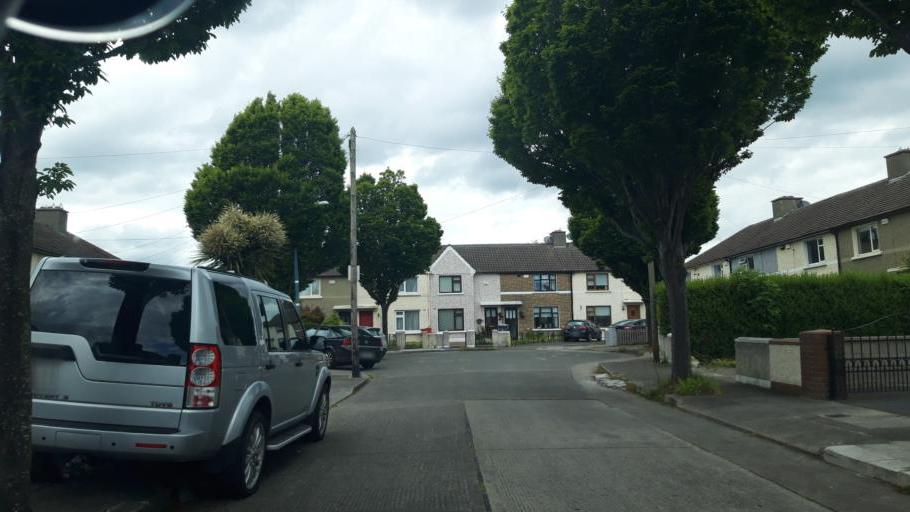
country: IE
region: Leinster
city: Dollymount
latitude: 53.3606
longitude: -6.1906
